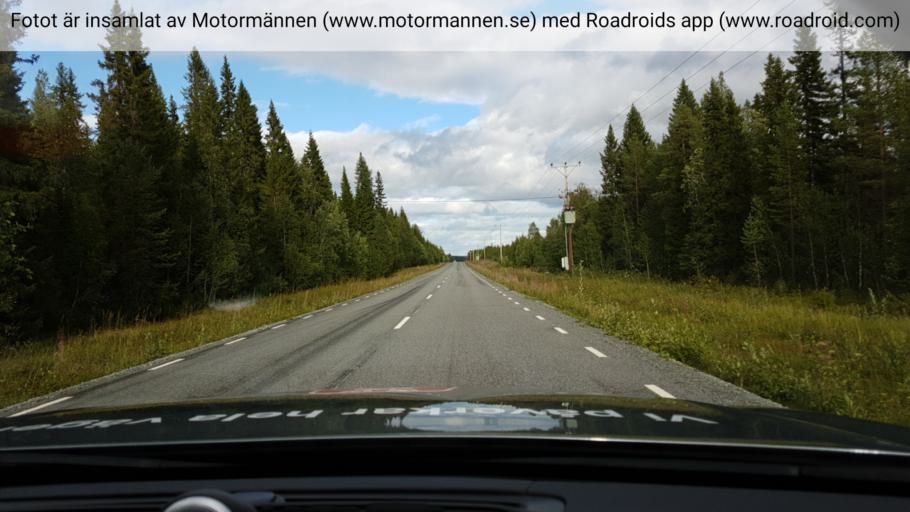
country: SE
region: Jaemtland
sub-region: Krokoms Kommun
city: Krokom
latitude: 63.6636
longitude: 14.5088
